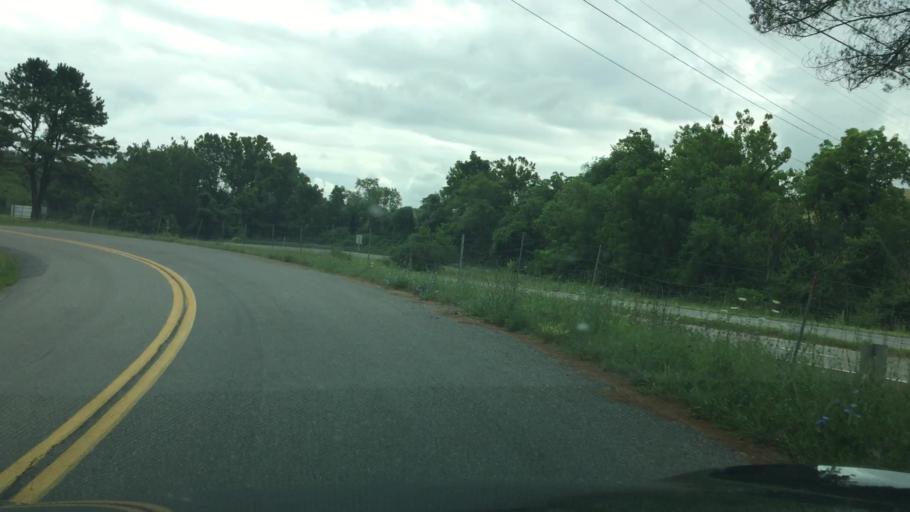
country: US
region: Virginia
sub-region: Pulaski County
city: Pulaski
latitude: 36.9919
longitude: -80.7917
